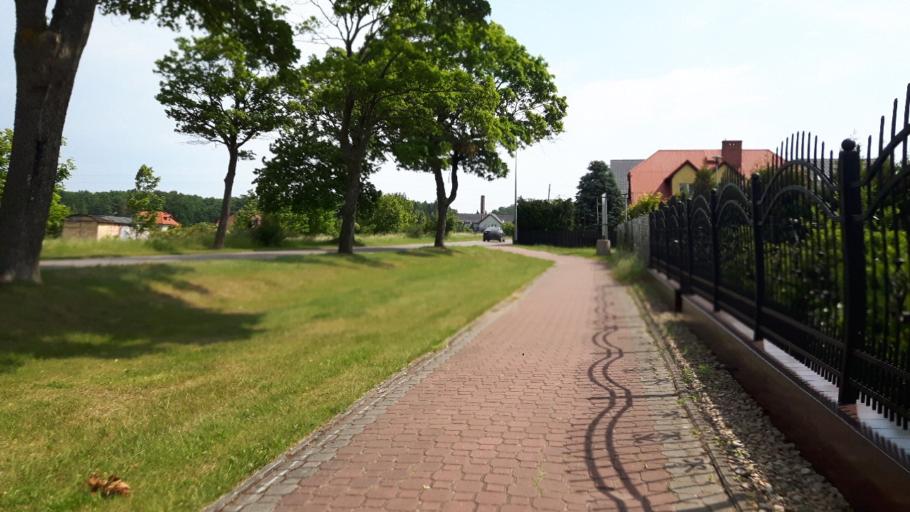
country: PL
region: Pomeranian Voivodeship
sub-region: Powiat leborski
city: Leba
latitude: 54.7515
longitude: 17.5800
